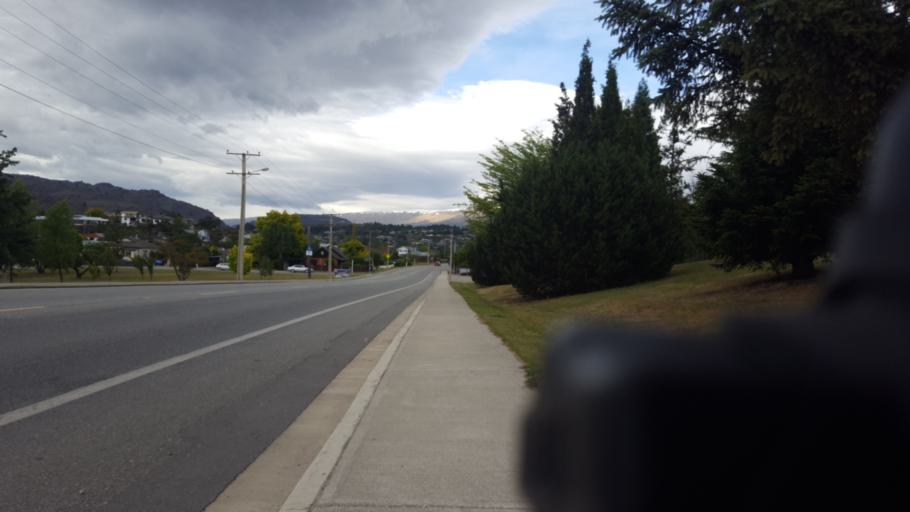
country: NZ
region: Otago
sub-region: Queenstown-Lakes District
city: Wanaka
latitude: -45.2472
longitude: 169.4012
